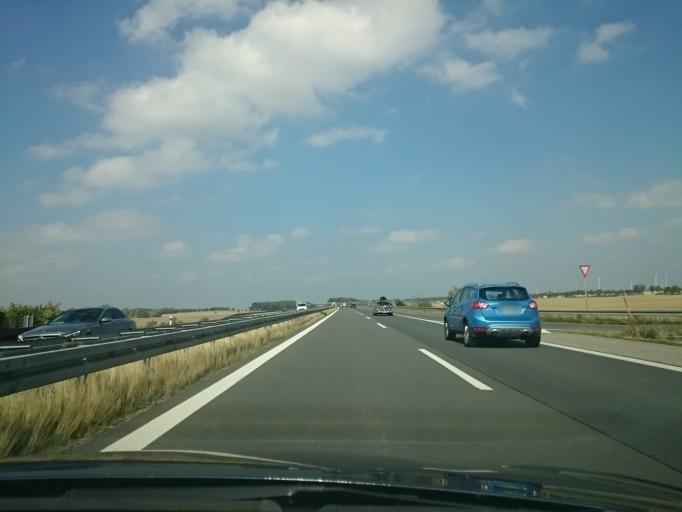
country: DE
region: Brandenburg
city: Schonfeld
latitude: 53.3954
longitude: 13.9936
